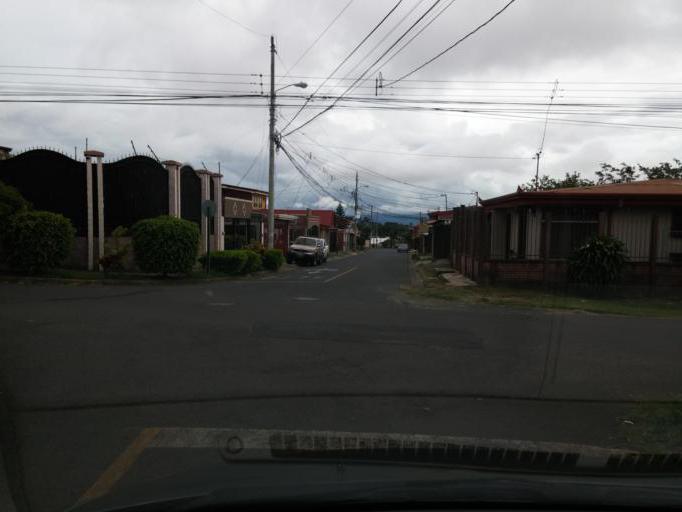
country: CR
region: Heredia
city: Mercedes
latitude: 10.0243
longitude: -84.1307
